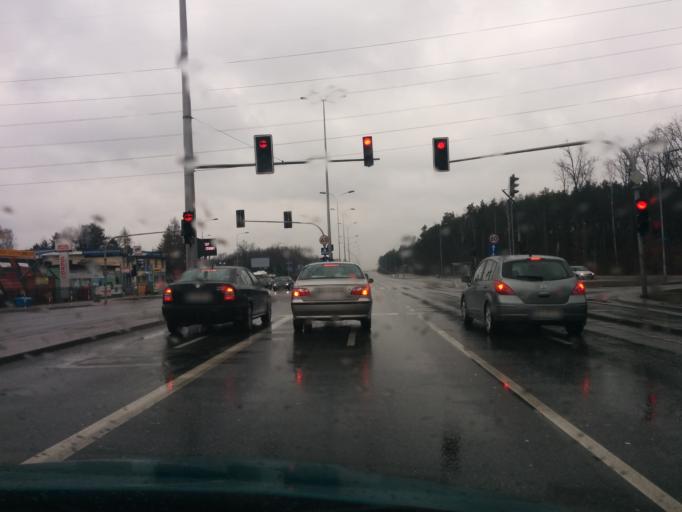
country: PL
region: Masovian Voivodeship
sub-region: Powiat legionowski
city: Jablonna
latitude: 52.3556
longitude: 20.9416
